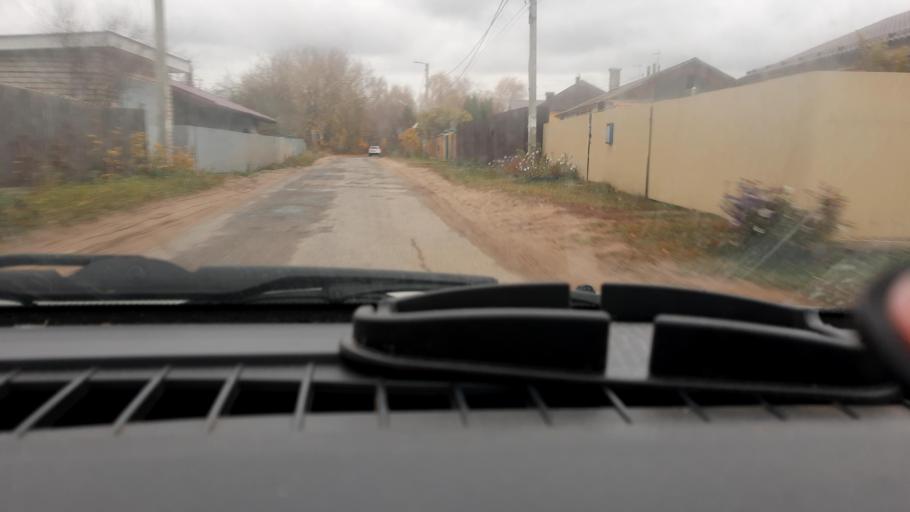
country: RU
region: Nizjnij Novgorod
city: Sitniki
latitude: 56.4146
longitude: 44.0384
